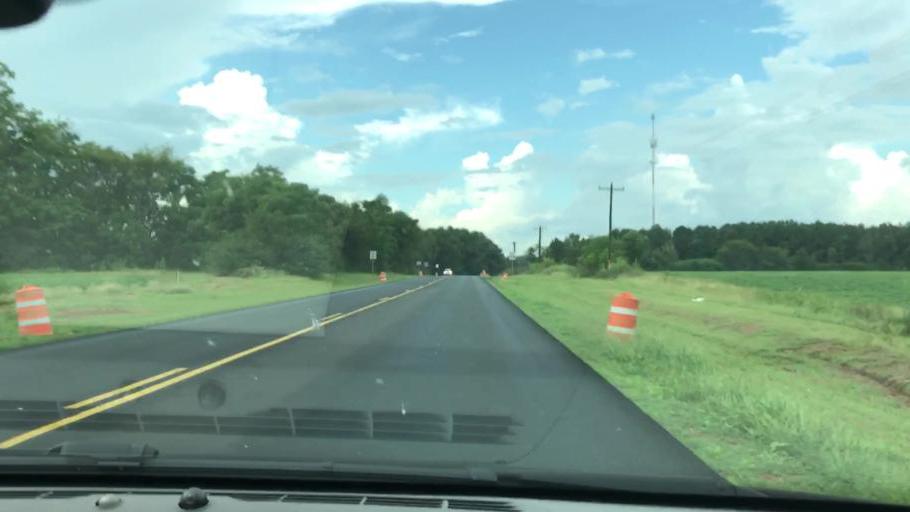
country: US
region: Georgia
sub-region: Early County
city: Blakely
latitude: 31.3987
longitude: -84.9556
